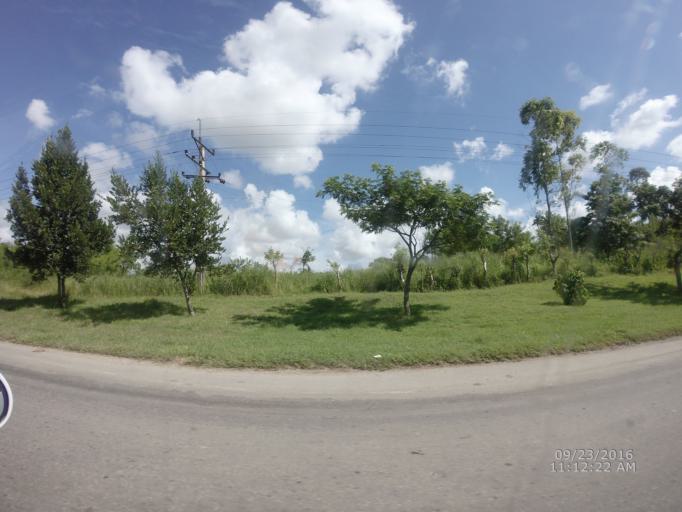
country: CU
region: La Habana
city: Arroyo Naranjo
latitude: 23.0292
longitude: -82.2827
